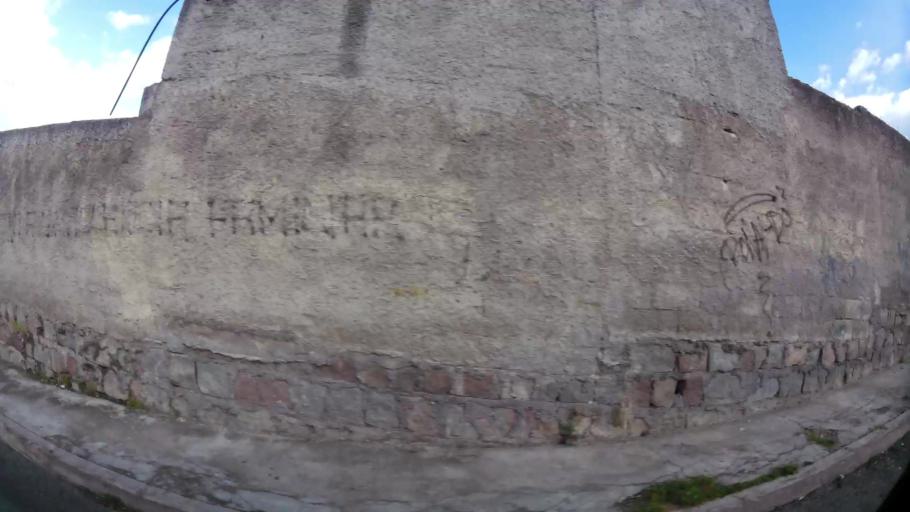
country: EC
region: Pichincha
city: Quito
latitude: -0.1351
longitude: -78.4595
